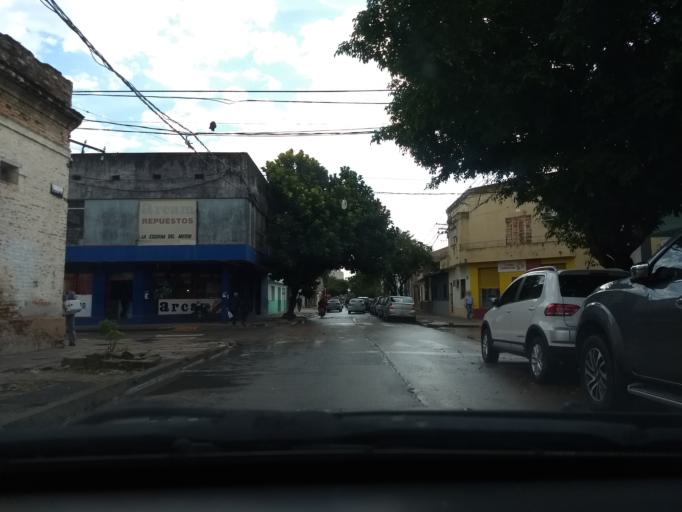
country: AR
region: Corrientes
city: Corrientes
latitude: -27.4719
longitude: -58.8283
